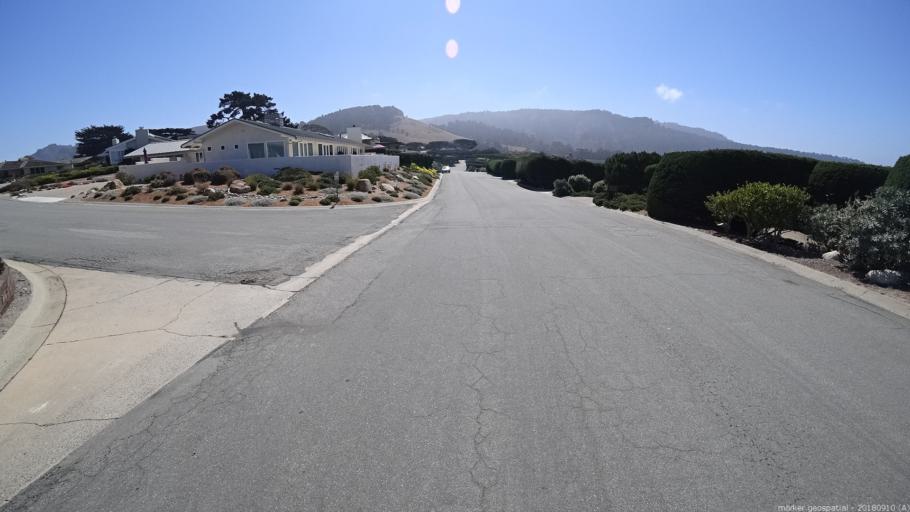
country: US
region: California
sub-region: Monterey County
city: Carmel-by-the-Sea
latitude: 36.5327
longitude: -121.9257
